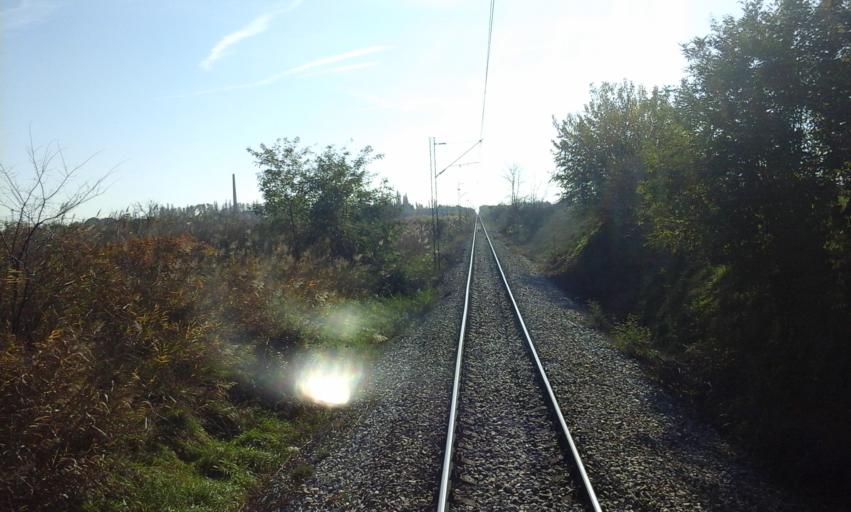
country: RS
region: Autonomna Pokrajina Vojvodina
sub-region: Severnobacki Okrug
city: Subotica
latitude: 46.0769
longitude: 19.6894
